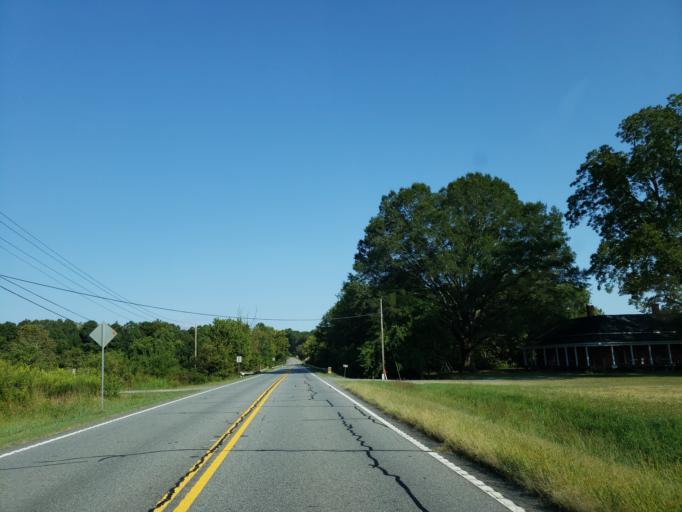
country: US
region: Georgia
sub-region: Whitfield County
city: Varnell
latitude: 34.8965
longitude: -84.9247
